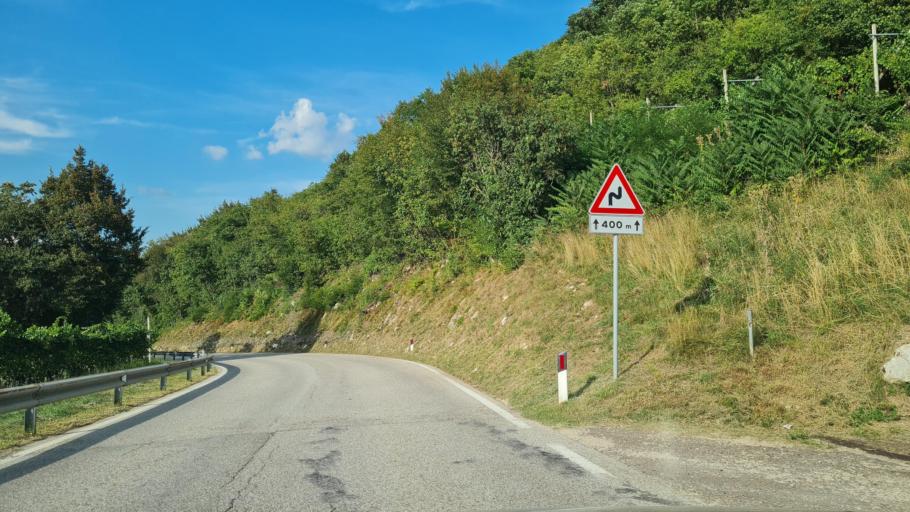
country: IT
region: Trentino-Alto Adige
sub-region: Provincia di Trento
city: Mattarello
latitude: 46.0223
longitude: 11.1453
